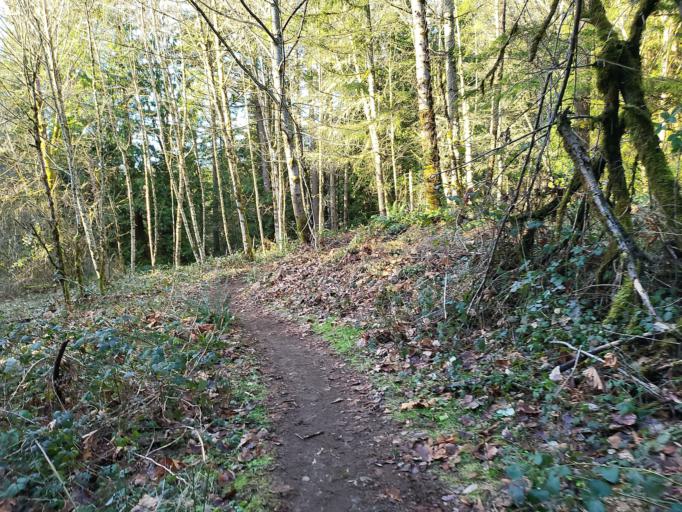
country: US
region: Washington
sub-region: King County
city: Issaquah
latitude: 47.5244
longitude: -122.0241
